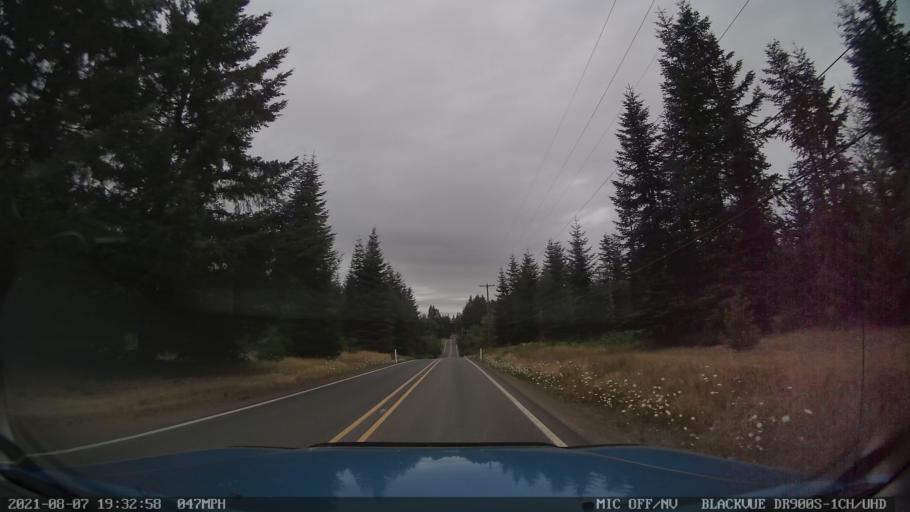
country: US
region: Oregon
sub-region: Linn County
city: Lyons
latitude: 44.9042
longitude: -122.6499
